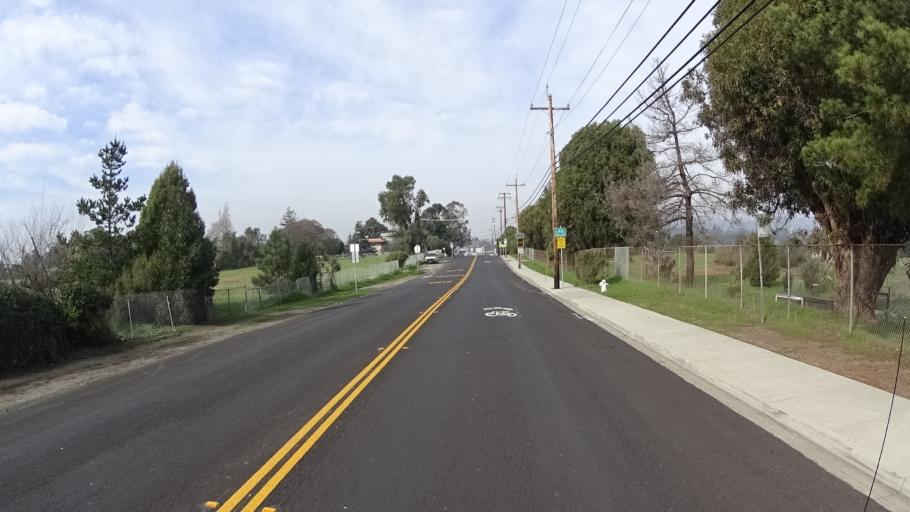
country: US
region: California
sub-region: Alameda County
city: Hayward
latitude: 37.6695
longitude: -122.0708
